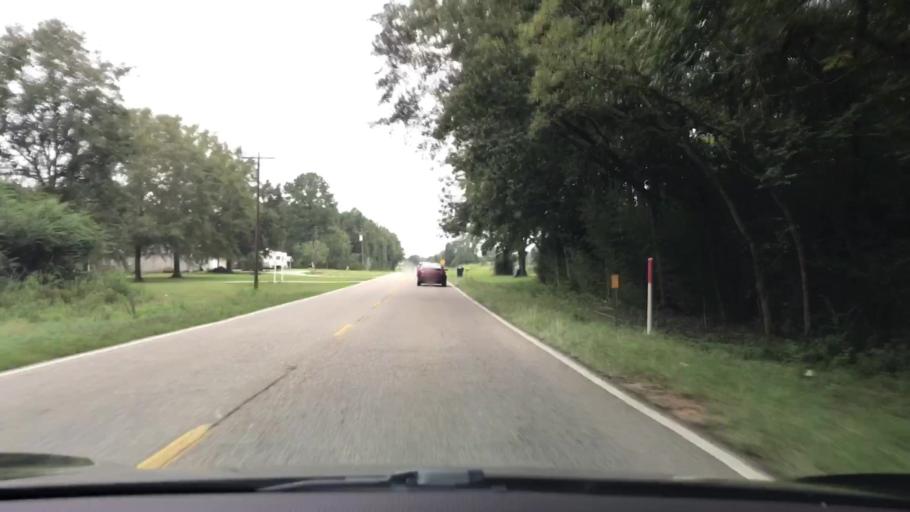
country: US
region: Alabama
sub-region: Geneva County
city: Samson
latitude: 31.1705
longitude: -86.1434
